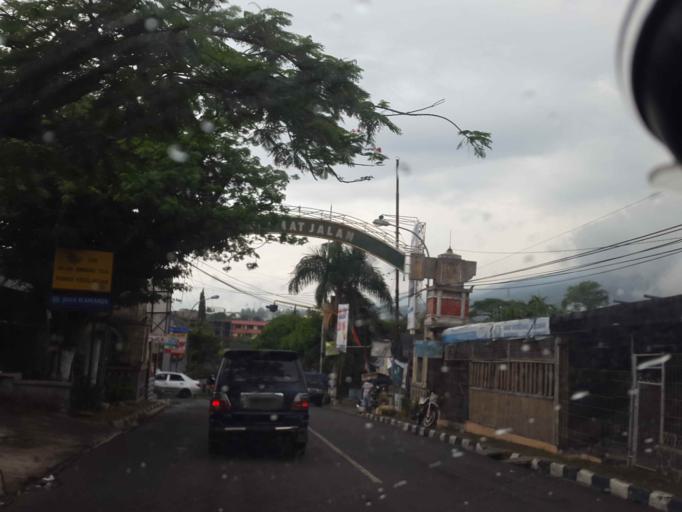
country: ID
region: East Java
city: Batu
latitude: -7.8624
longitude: 112.5268
